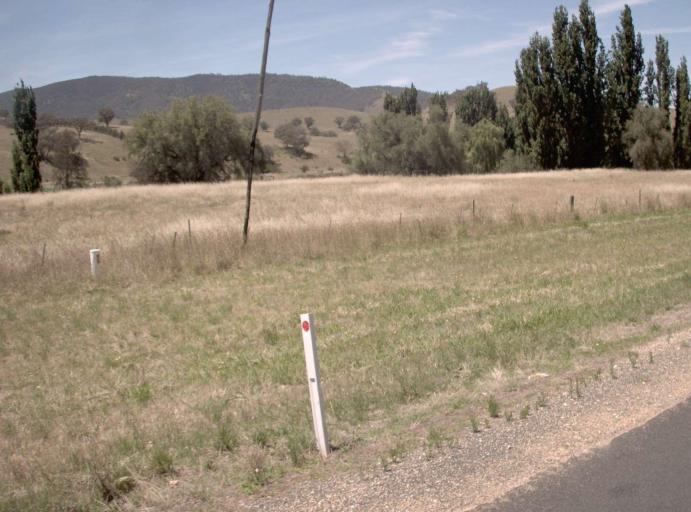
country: AU
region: Victoria
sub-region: East Gippsland
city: Bairnsdale
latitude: -37.1931
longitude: 147.7242
